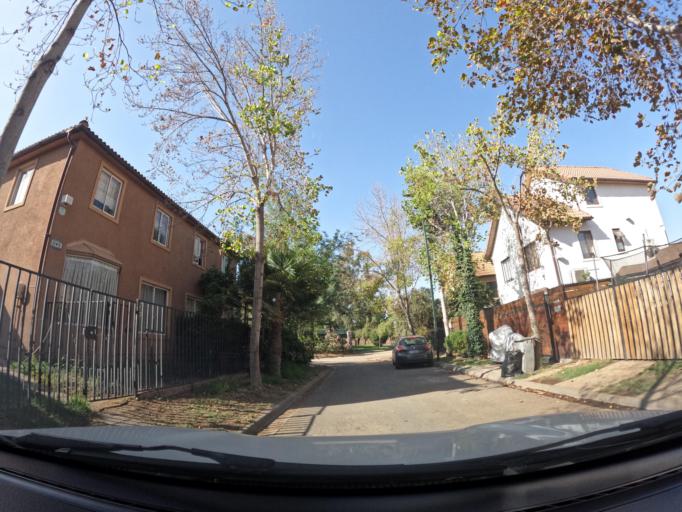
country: CL
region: Santiago Metropolitan
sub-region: Provincia de Santiago
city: Villa Presidente Frei, Nunoa, Santiago, Chile
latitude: -33.5115
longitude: -70.5467
